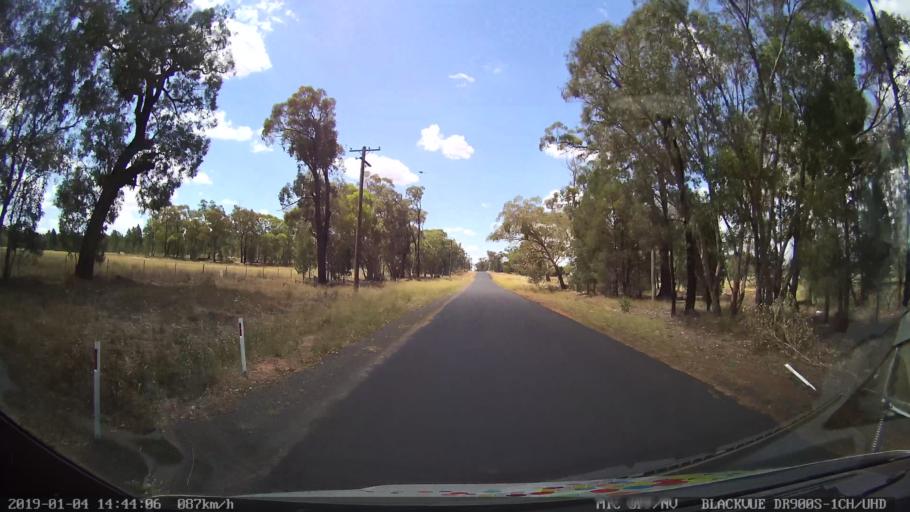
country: AU
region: New South Wales
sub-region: Dubbo Municipality
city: Dubbo
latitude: -32.1106
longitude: 148.6549
